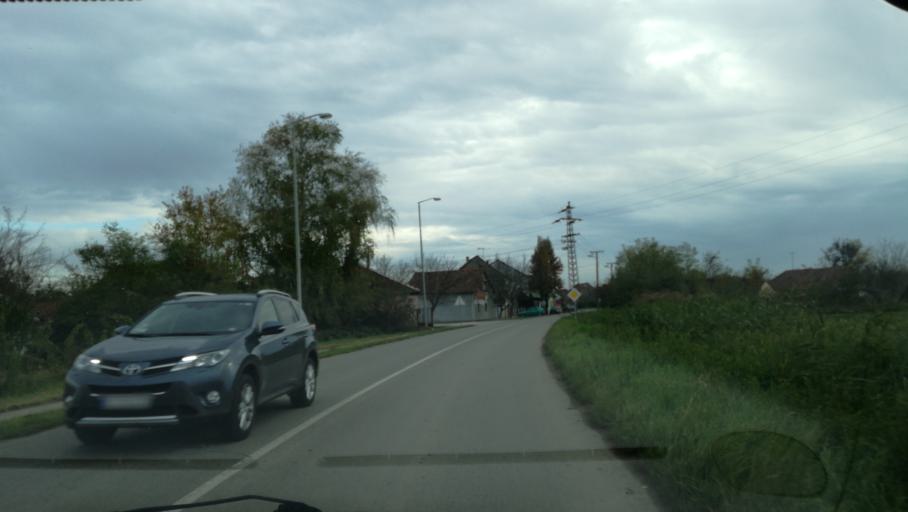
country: RS
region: Autonomna Pokrajina Vojvodina
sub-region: Severnobanatski Okrug
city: Kikinda
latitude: 45.8436
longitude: 20.4689
